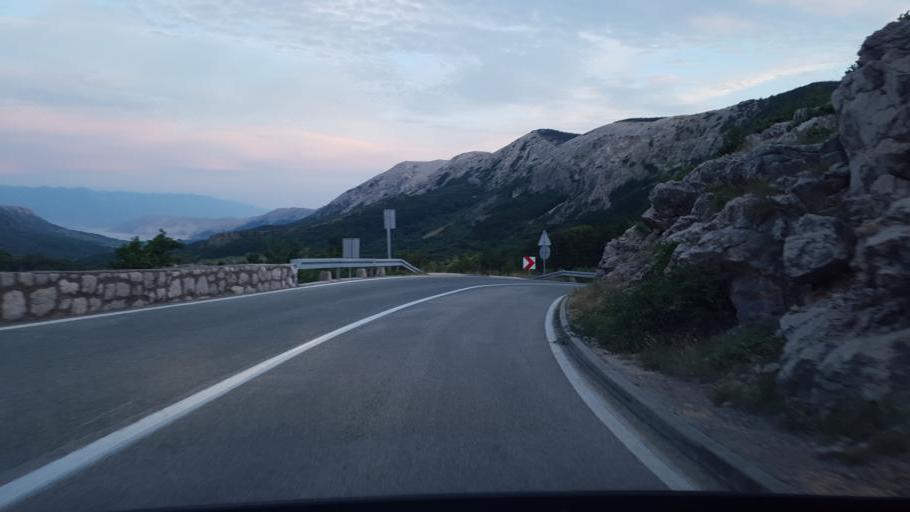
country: HR
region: Primorsko-Goranska
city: Punat
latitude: 45.0280
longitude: 14.6780
